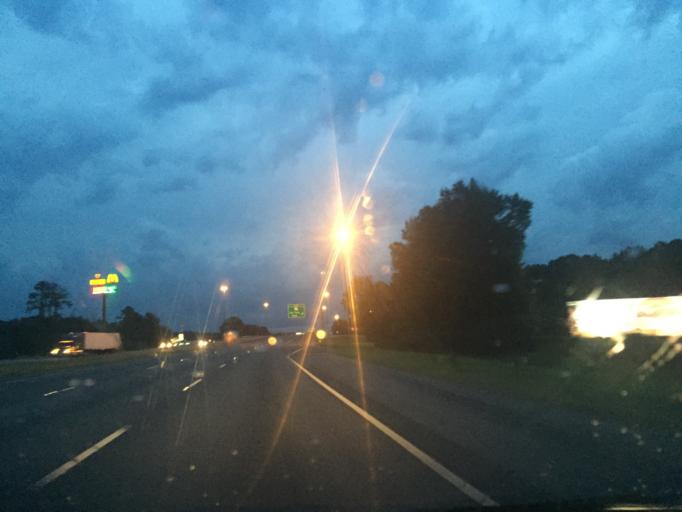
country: US
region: Georgia
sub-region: Bryan County
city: Richmond Hill
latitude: 31.9564
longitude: -81.3324
